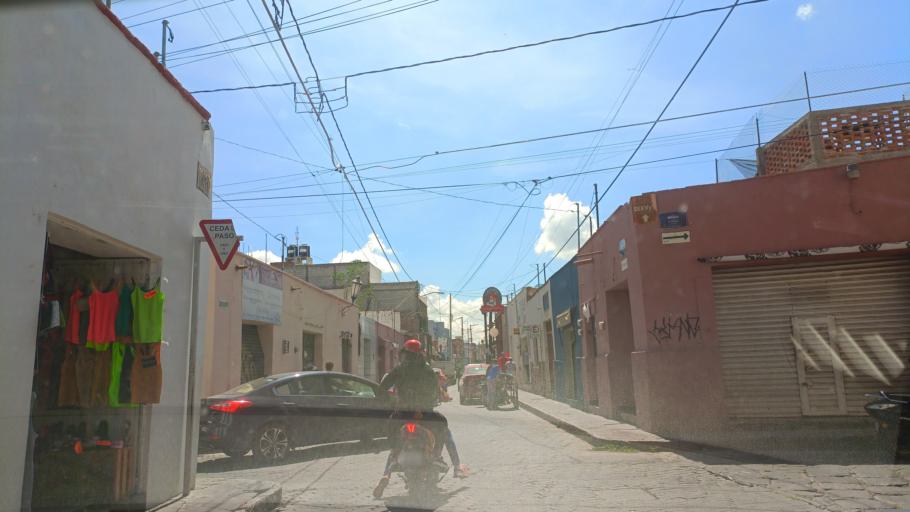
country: MX
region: Guerrero
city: San Luis de la Paz
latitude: 21.2974
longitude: -100.5185
